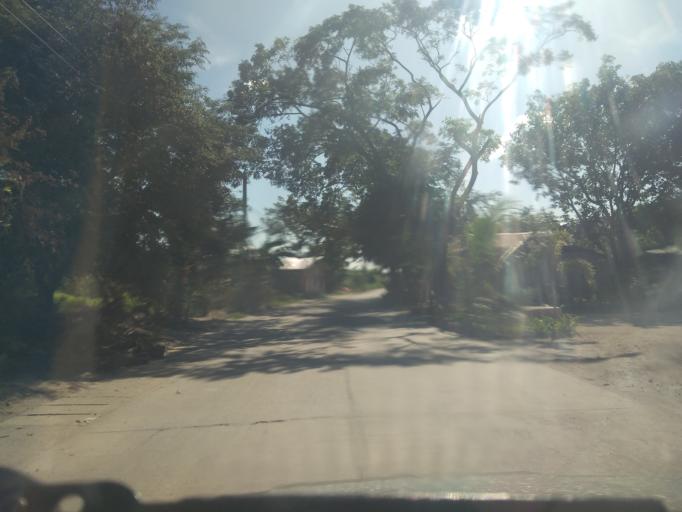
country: PH
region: Central Luzon
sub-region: Province of Pampanga
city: Calibutbut
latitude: 15.0872
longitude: 120.6032
